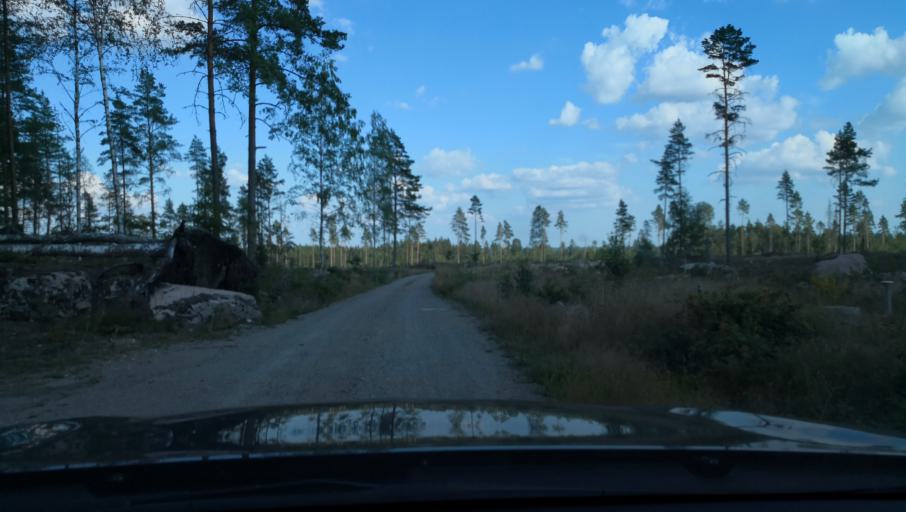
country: SE
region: Vaestmanland
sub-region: Vasteras
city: Skultuna
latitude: 59.7093
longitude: 16.3815
